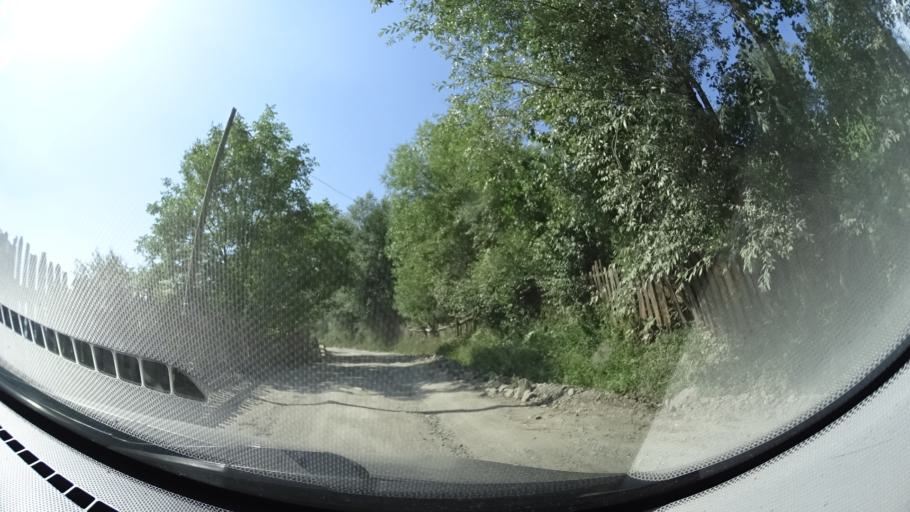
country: GE
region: Ajaria
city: Dioknisi
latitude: 41.6464
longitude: 42.4596
